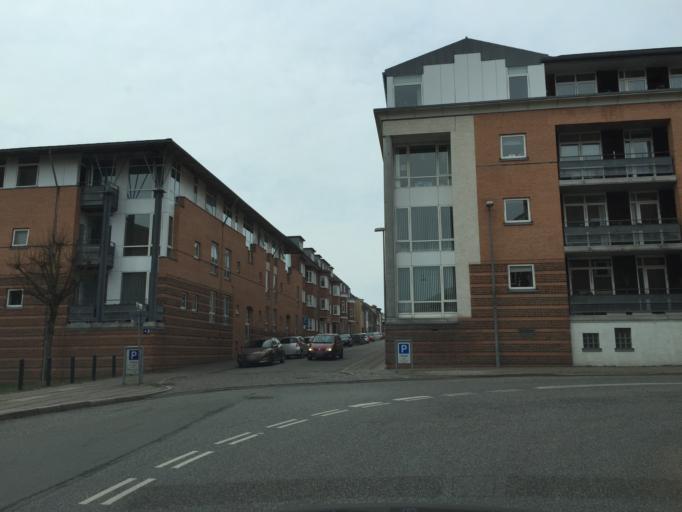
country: DK
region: South Denmark
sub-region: Kolding Kommune
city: Kolding
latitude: 55.4895
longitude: 9.4705
